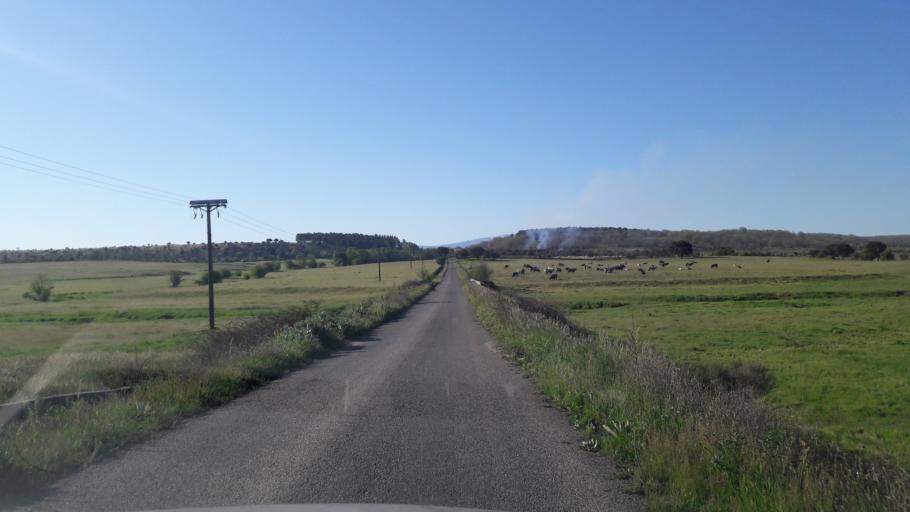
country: ES
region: Castille and Leon
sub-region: Provincia de Salamanca
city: Endrinal
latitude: 40.6113
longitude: -5.8221
